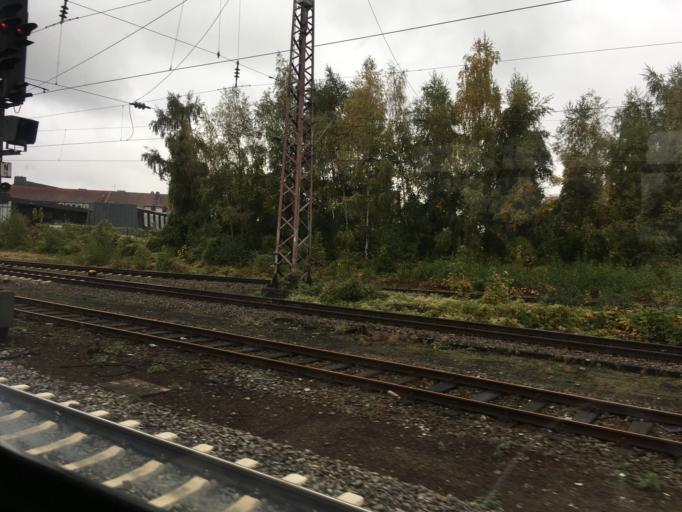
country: DE
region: Lower Saxony
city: Osnabrueck
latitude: 52.2747
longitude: 8.0572
